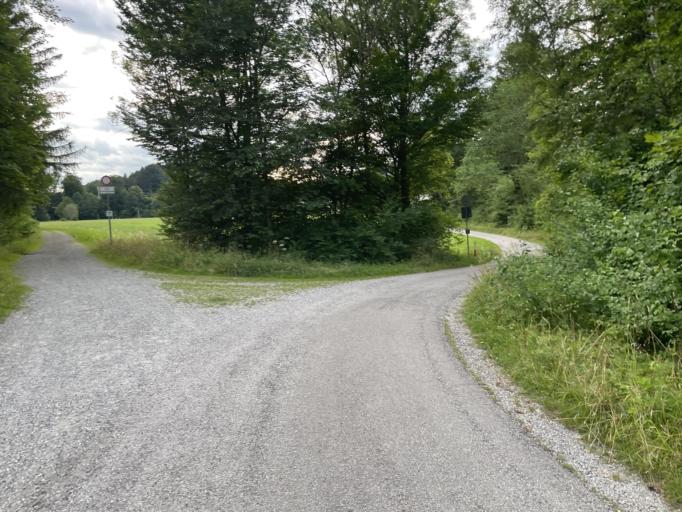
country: DE
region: Bavaria
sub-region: Upper Bavaria
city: Peissenberg
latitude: 47.7784
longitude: 11.0572
